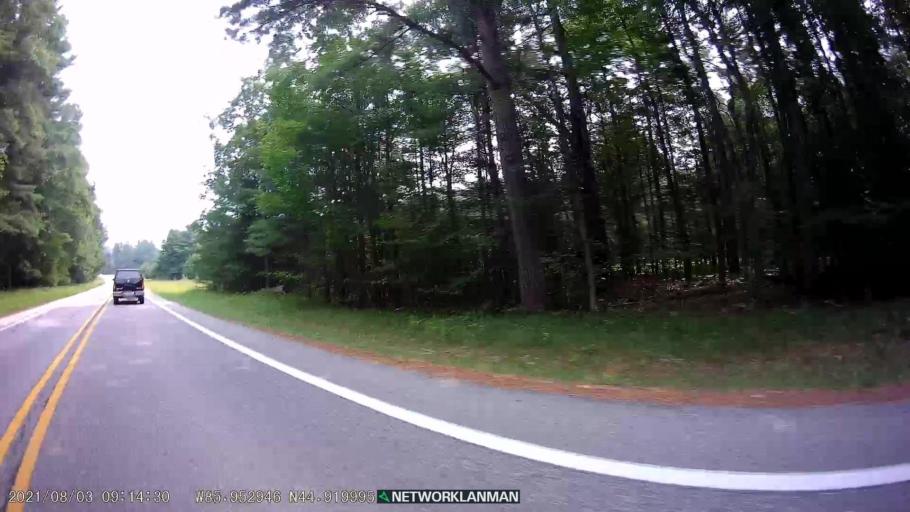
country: US
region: Michigan
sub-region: Leelanau County
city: Leland
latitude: 44.9202
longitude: -85.9526
